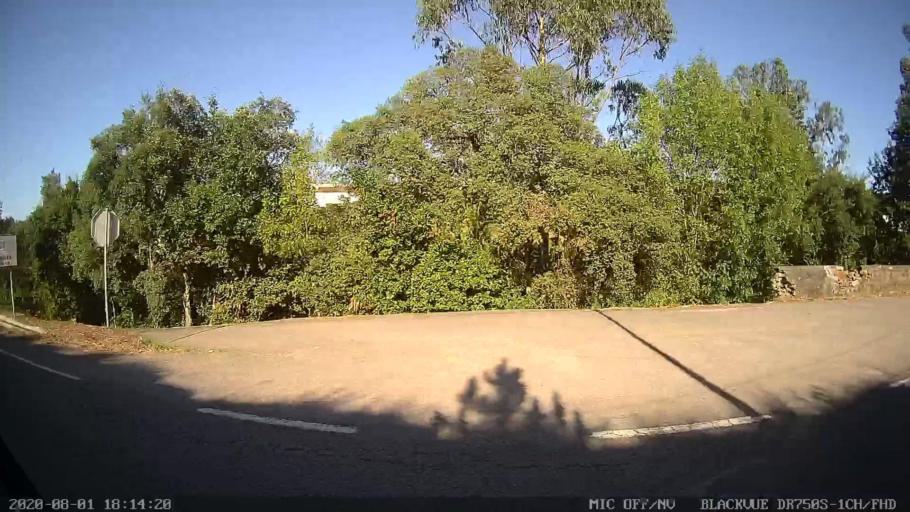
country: PT
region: Porto
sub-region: Pacos de Ferreira
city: Seroa
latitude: 41.2716
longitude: -8.4699
